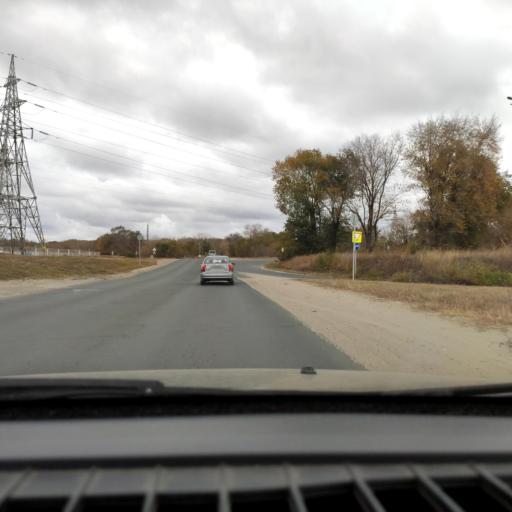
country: RU
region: Samara
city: Tol'yatti
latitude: 53.5654
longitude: 49.2899
